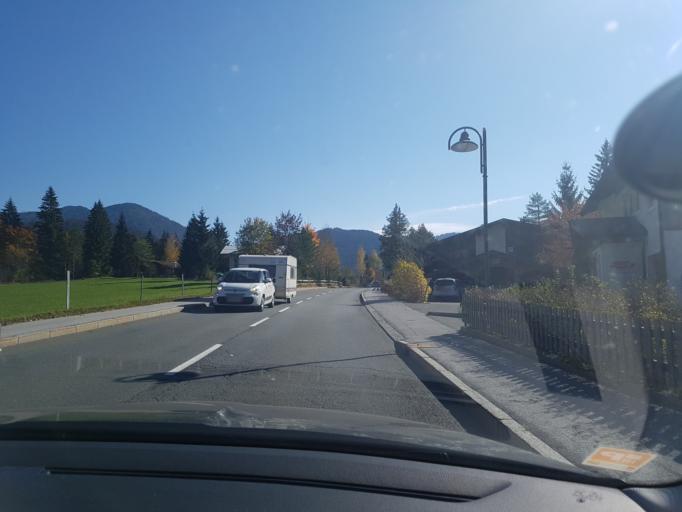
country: AT
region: Tyrol
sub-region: Politischer Bezirk Kitzbuhel
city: Fieberbrunn
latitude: 47.5242
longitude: 12.5768
